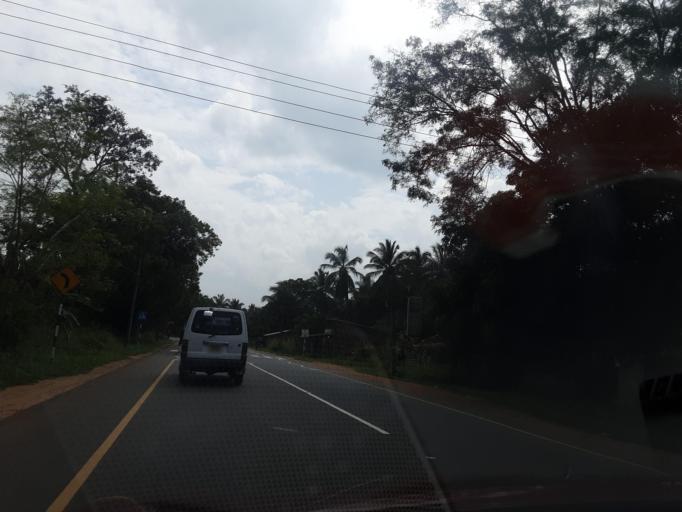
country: LK
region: North Central
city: Anuradhapura
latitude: 8.4823
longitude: 80.5097
